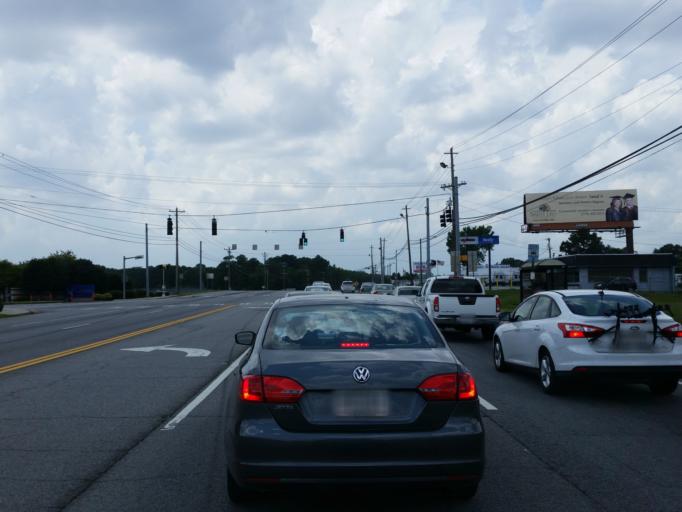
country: US
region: Georgia
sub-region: Cobb County
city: Smyrna
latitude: 33.9194
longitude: -84.5026
